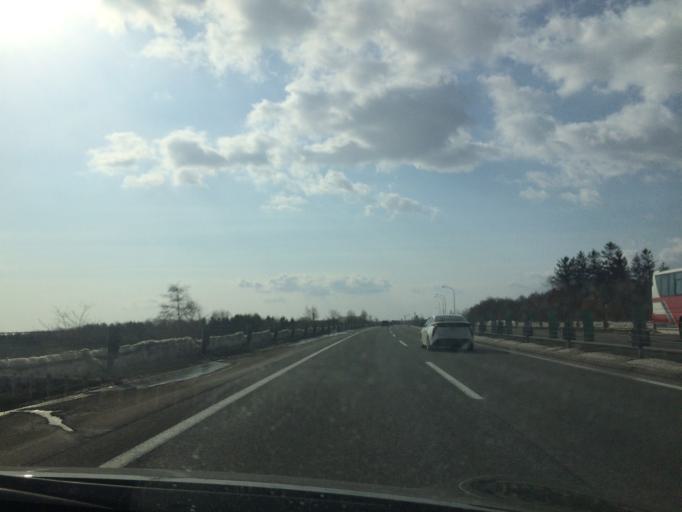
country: JP
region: Hokkaido
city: Kitahiroshima
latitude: 42.9122
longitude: 141.5494
